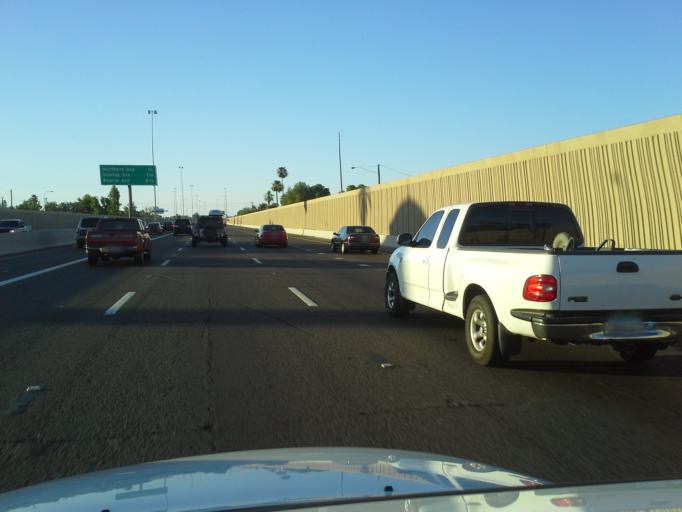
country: US
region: Arizona
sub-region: Maricopa County
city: Glendale
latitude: 33.5449
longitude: -112.1123
